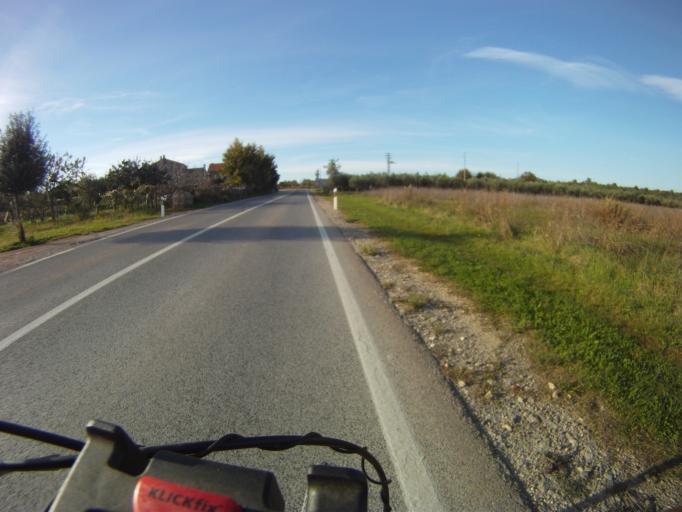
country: HR
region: Istarska
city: Novigrad
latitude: 45.3207
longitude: 13.5858
